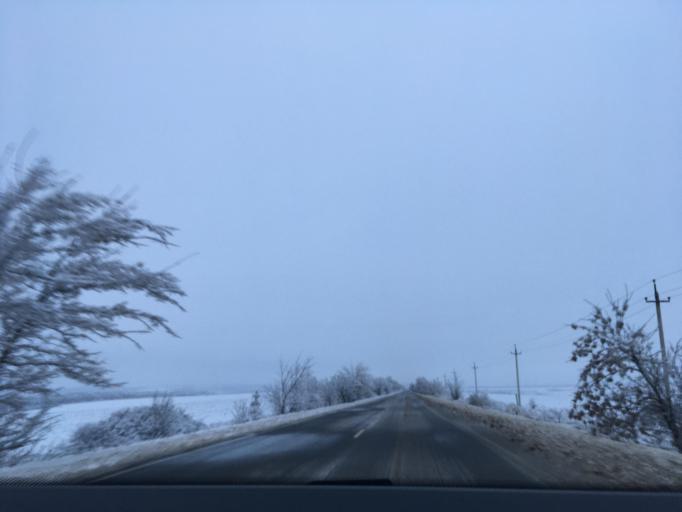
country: RU
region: Voronezj
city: Verkhniy Mamon
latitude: 50.0224
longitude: 40.0897
